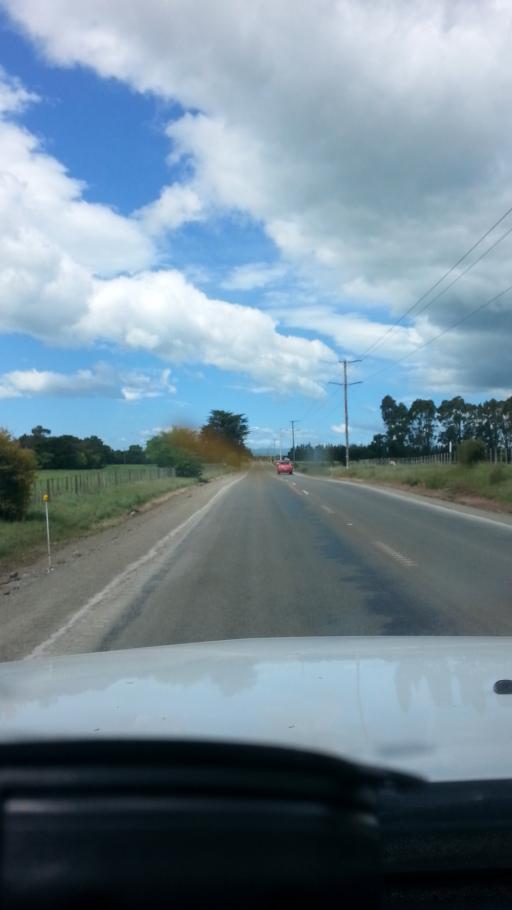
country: NZ
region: Wellington
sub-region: Masterton District
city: Masterton
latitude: -40.8334
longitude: 175.6284
